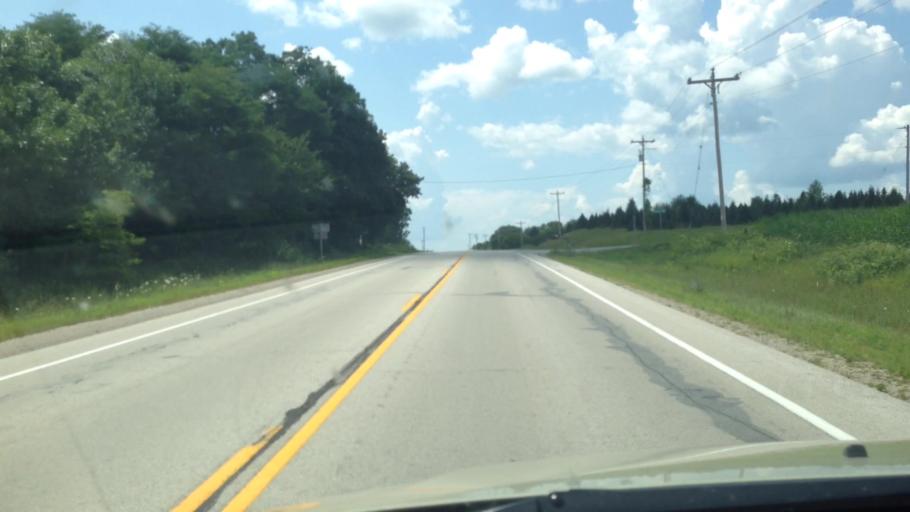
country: US
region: Wisconsin
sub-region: Brown County
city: Suamico
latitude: 44.6481
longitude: -88.1300
